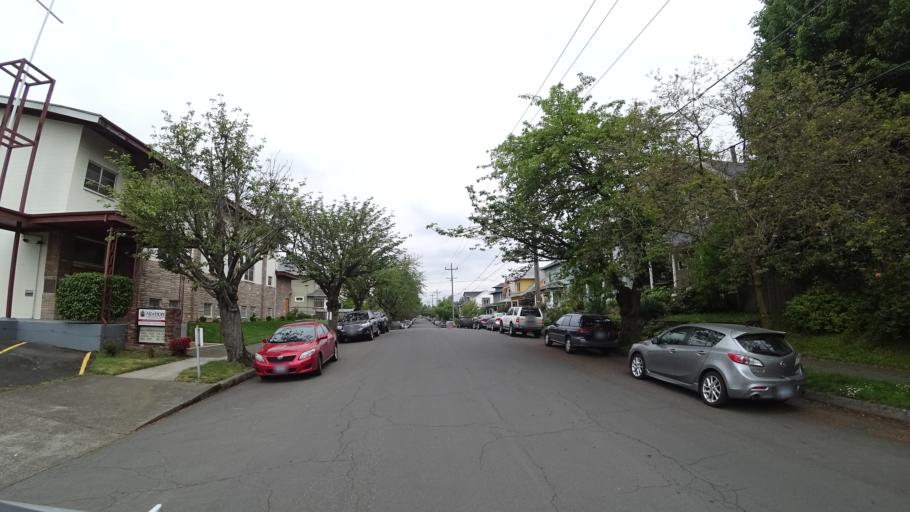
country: US
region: Oregon
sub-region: Multnomah County
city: Portland
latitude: 45.5500
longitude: -122.6691
